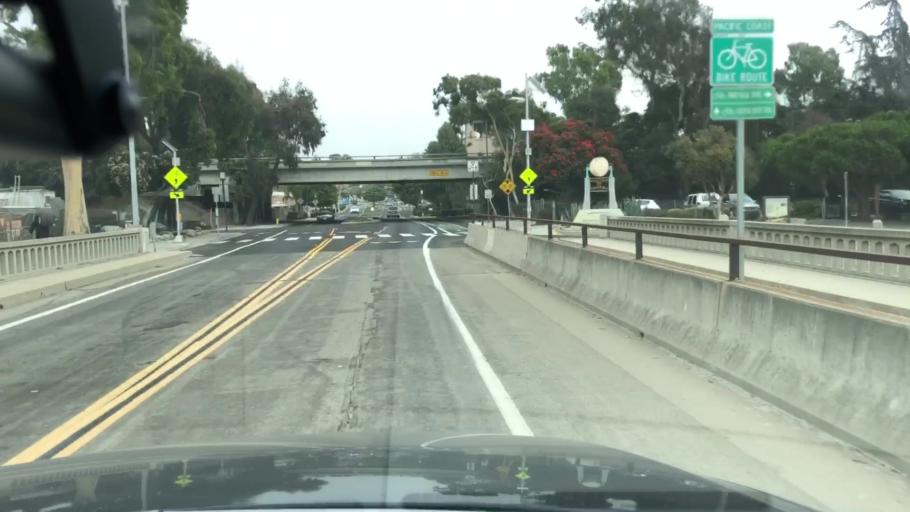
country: US
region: California
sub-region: Ventura County
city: Ventura
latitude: 34.2818
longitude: -119.3068
